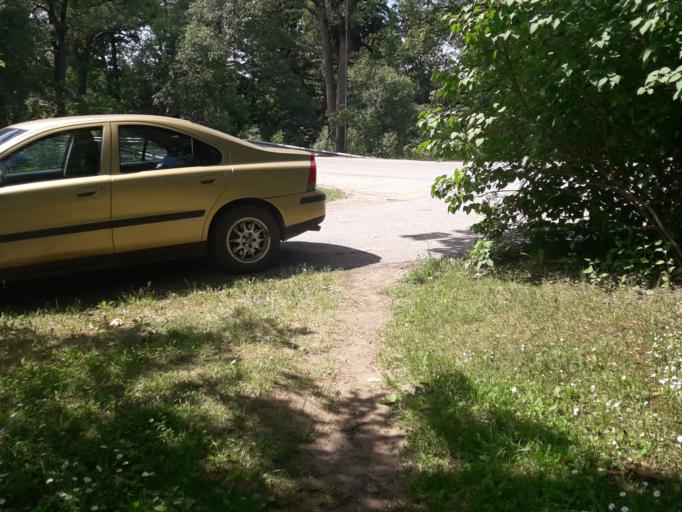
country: LV
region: Pargaujas
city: Stalbe
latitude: 57.3541
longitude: 24.9488
